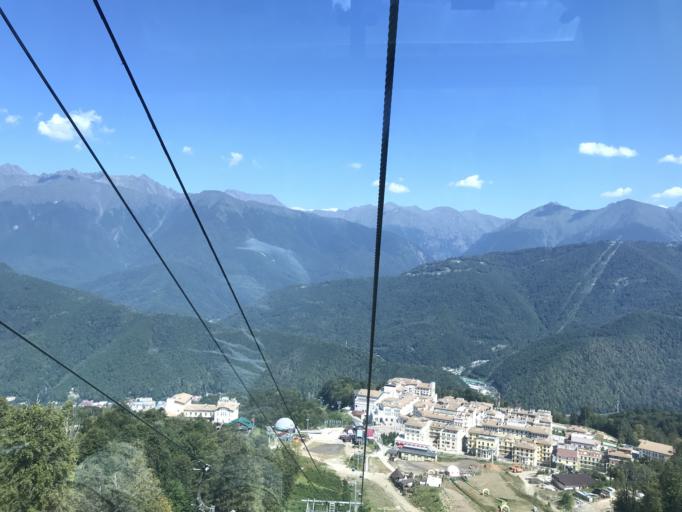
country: RU
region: Krasnodarskiy
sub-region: Sochi City
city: Krasnaya Polyana
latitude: 43.6645
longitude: 40.2554
